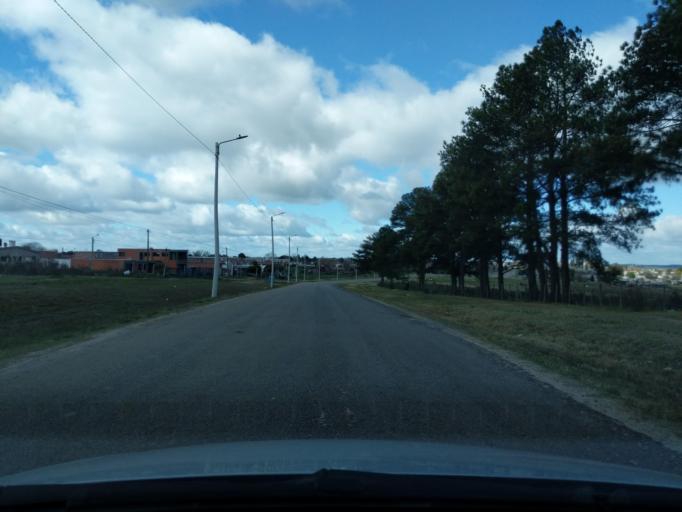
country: UY
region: Florida
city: Florida
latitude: -34.0794
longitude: -56.2283
